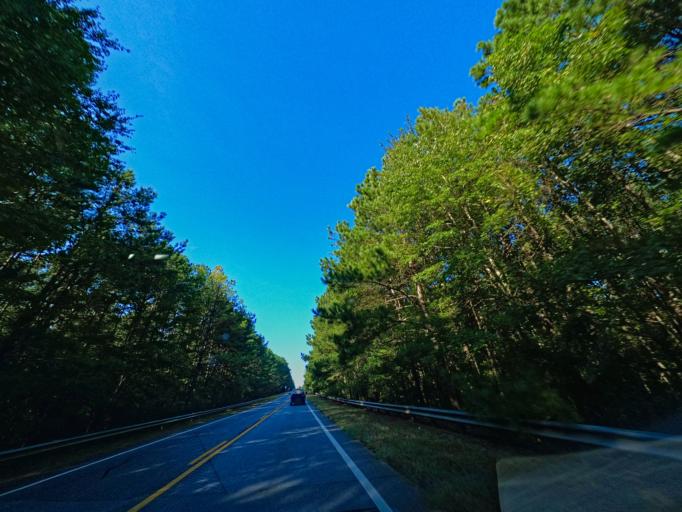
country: US
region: Georgia
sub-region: Coweta County
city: Newnan
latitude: 33.3922
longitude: -84.8404
